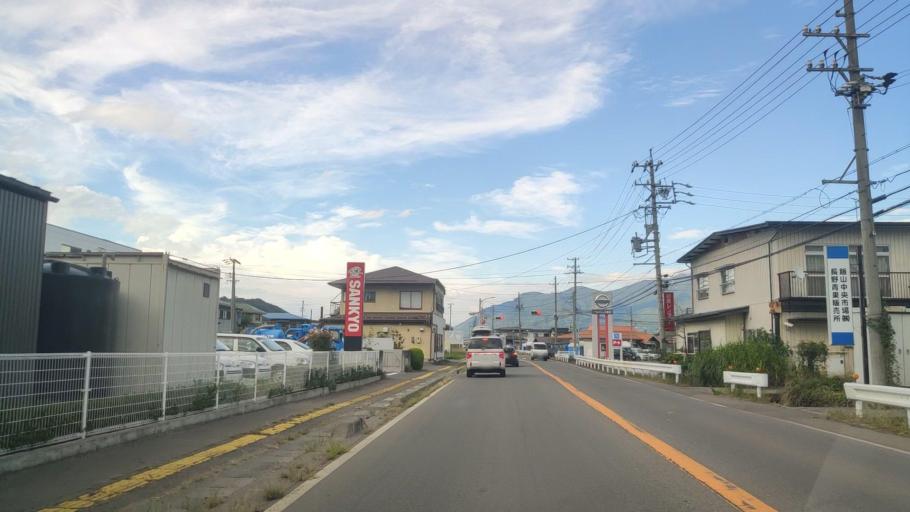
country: JP
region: Nagano
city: Nakano
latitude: 36.7325
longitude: 138.3430
